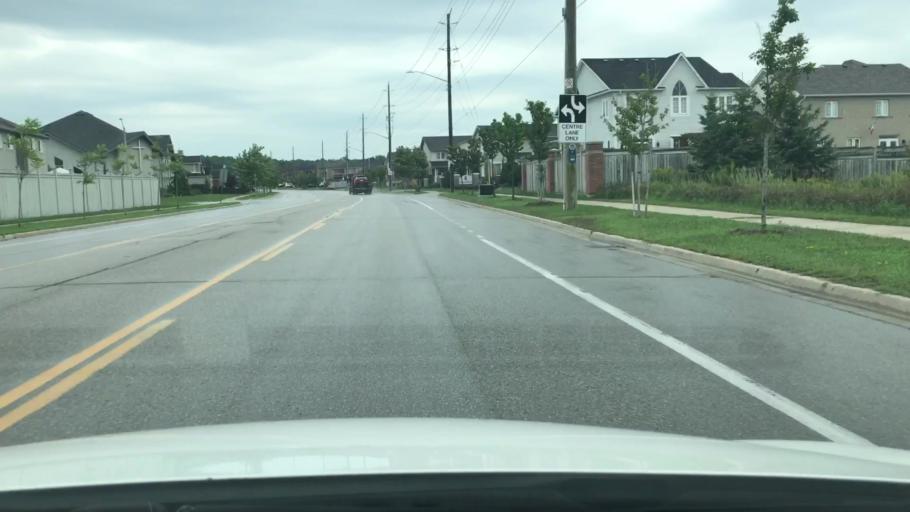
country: CA
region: Ontario
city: Innisfil
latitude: 44.3577
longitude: -79.6122
